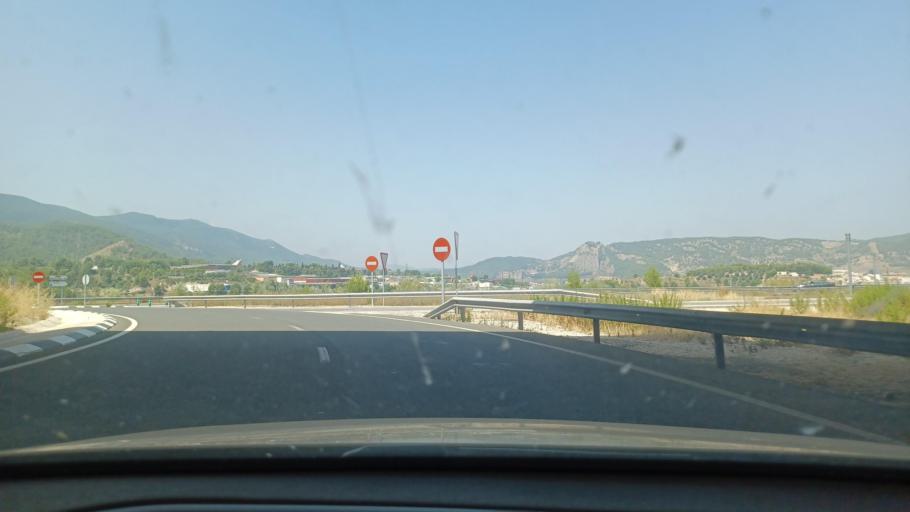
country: ES
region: Valencia
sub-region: Provincia de Alicante
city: Alcoy
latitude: 38.6843
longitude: -0.4607
